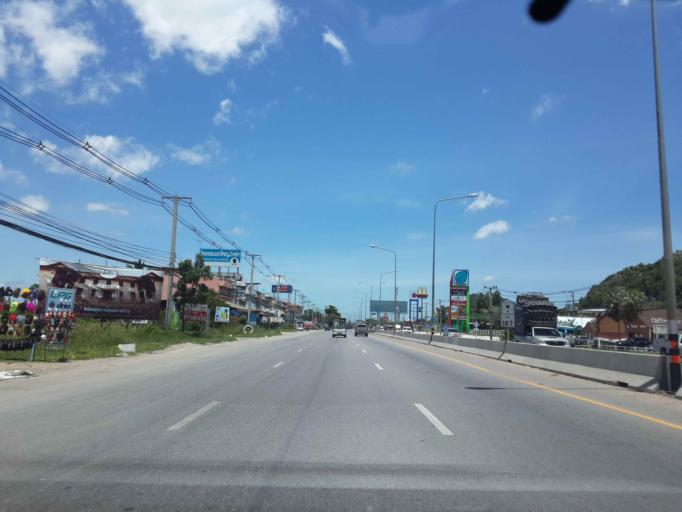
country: TH
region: Phetchaburi
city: Cha-am
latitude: 12.8156
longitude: 99.9413
